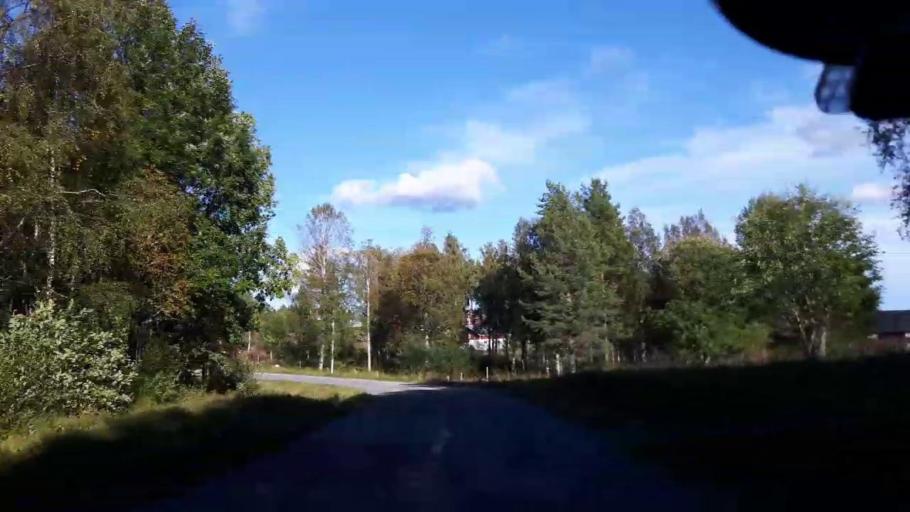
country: SE
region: Jaemtland
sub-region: Ragunda Kommun
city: Hammarstrand
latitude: 63.5281
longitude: 16.0778
